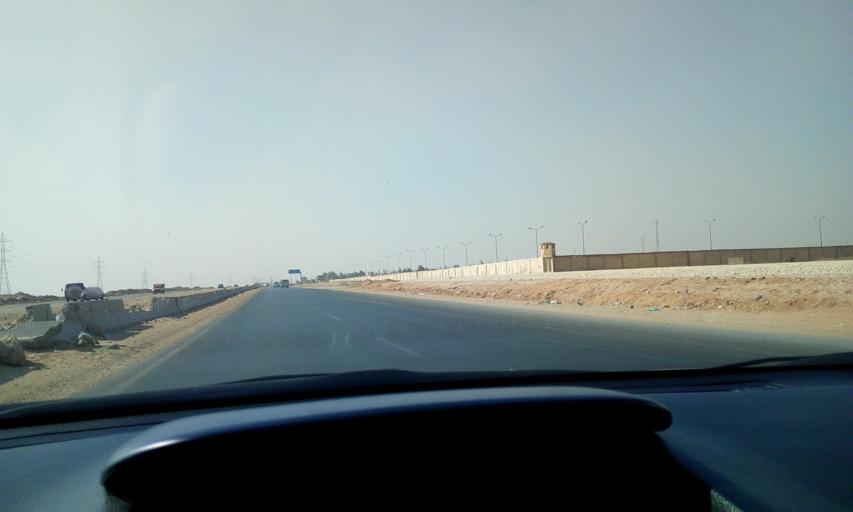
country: EG
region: Al Jizah
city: Madinat Sittah Uktubar
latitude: 29.8883
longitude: 31.0807
